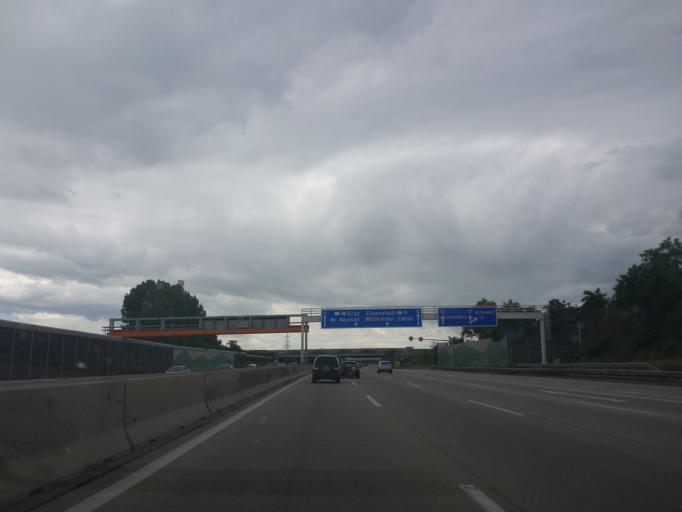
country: AT
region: Lower Austria
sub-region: Politischer Bezirk Modling
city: Biedermannsdorf
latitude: 48.0842
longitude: 16.3325
